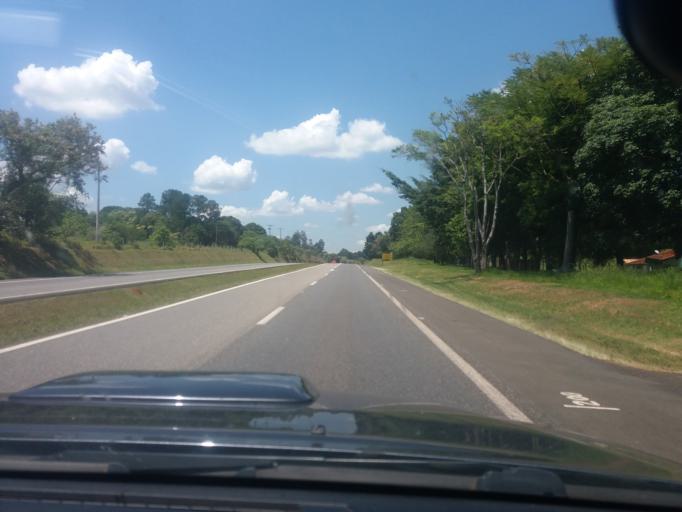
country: BR
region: Sao Paulo
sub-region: Tatui
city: Tatui
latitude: -23.4581
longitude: -47.9591
